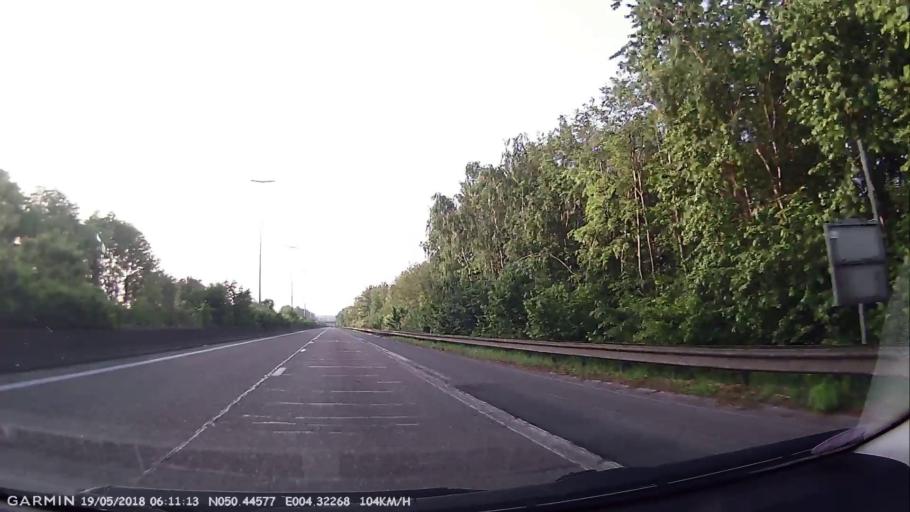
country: BE
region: Wallonia
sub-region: Province du Hainaut
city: Chapelle-lez-Herlaimont
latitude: 50.4457
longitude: 4.3228
